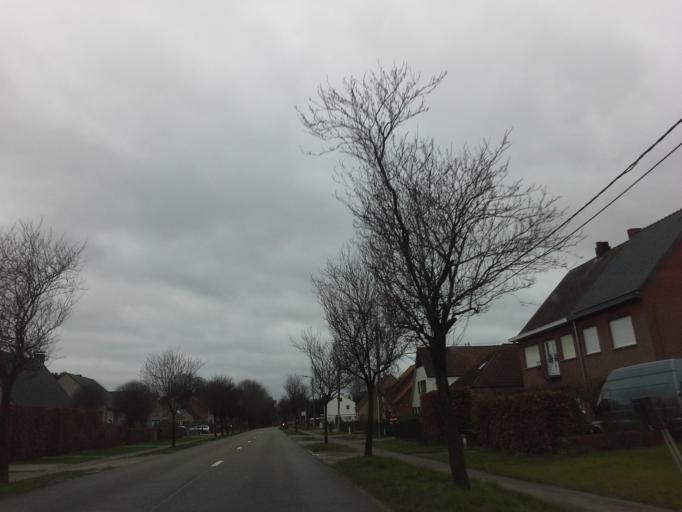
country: BE
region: Flanders
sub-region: Provincie Antwerpen
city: Olen
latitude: 51.1484
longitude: 4.8456
